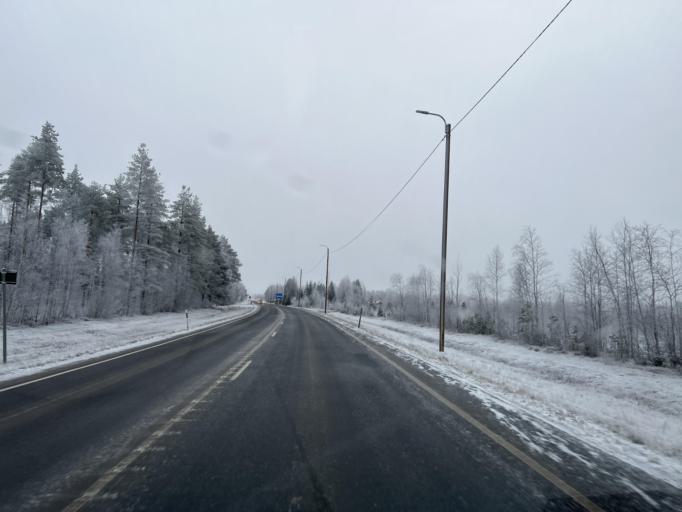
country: FI
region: Northern Ostrobothnia
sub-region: Oulunkaari
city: Utajaervi
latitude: 64.7482
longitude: 26.4311
